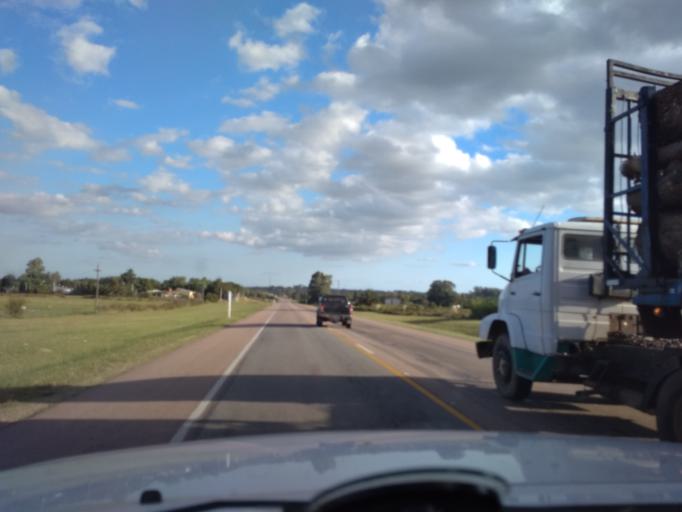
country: UY
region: Canelones
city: Canelones
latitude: -34.4902
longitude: -56.2819
